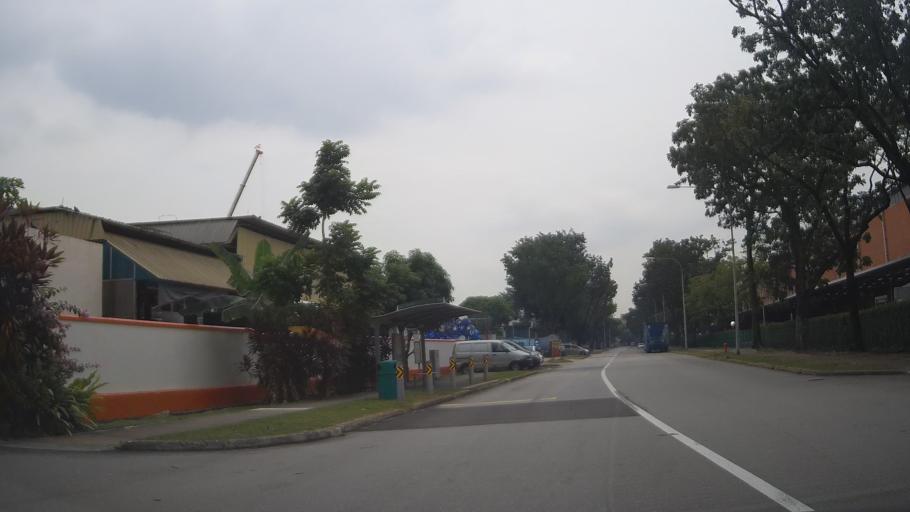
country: MY
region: Johor
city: Johor Bahru
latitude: 1.3133
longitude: 103.6596
